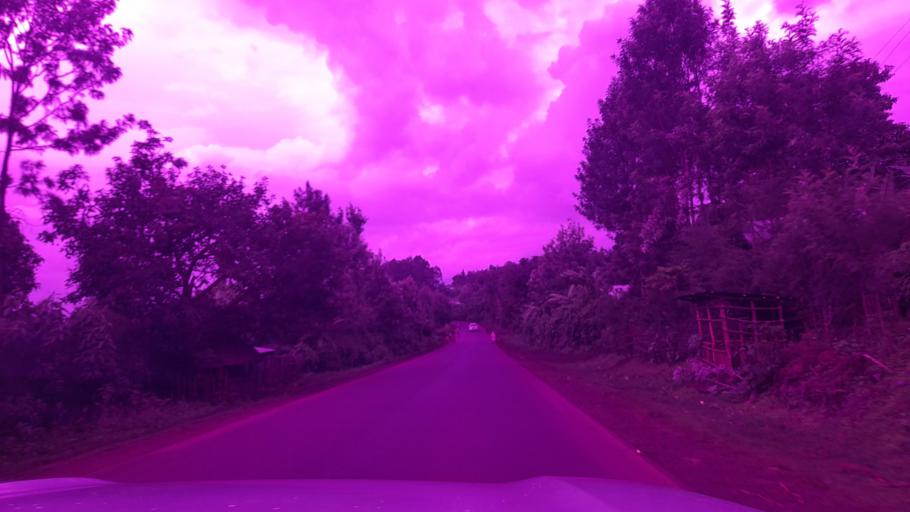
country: ET
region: Oromiya
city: Jima
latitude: 7.9060
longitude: 37.3921
